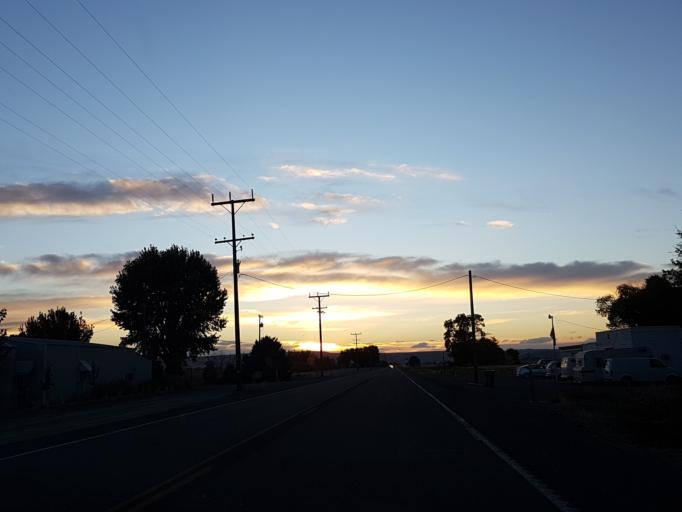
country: US
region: Oregon
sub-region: Malheur County
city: Vale
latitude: 43.9391
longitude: -117.3343
